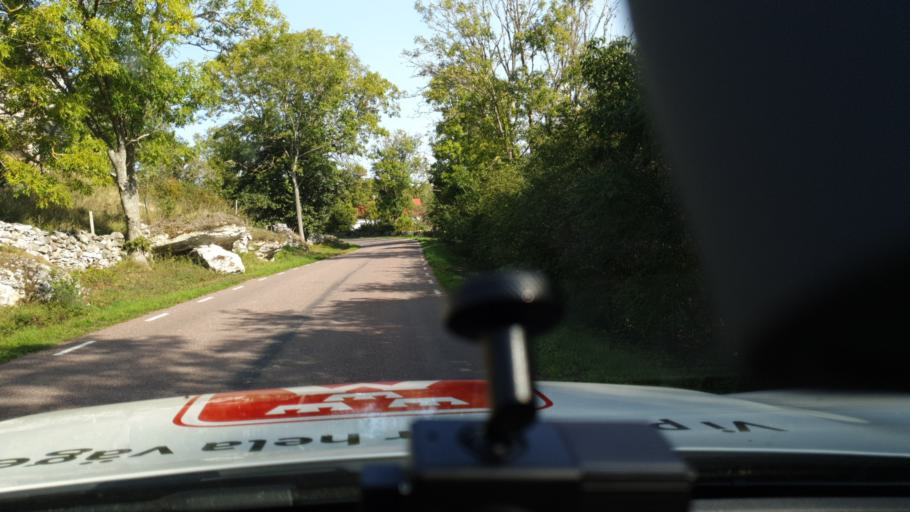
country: SE
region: Gotland
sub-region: Gotland
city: Hemse
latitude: 56.9207
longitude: 18.1587
